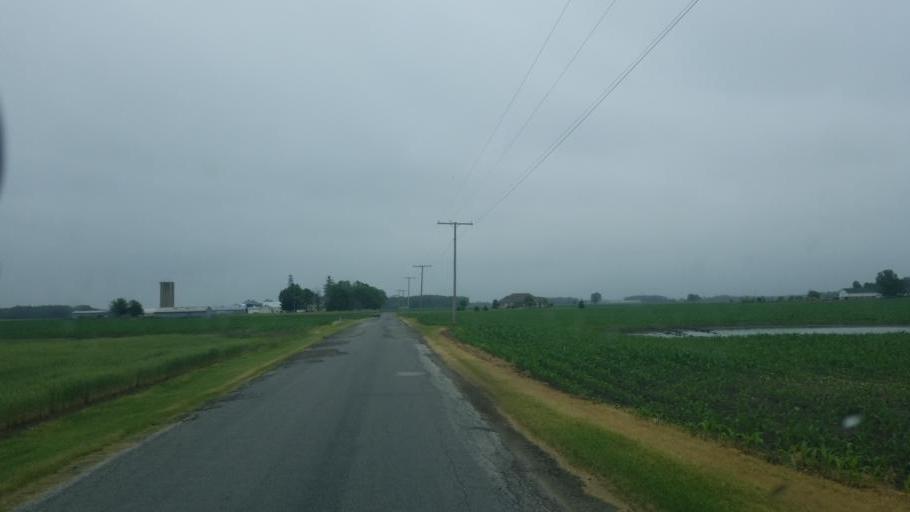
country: US
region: Indiana
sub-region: Marshall County
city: Bremen
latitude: 41.5079
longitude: -86.1231
